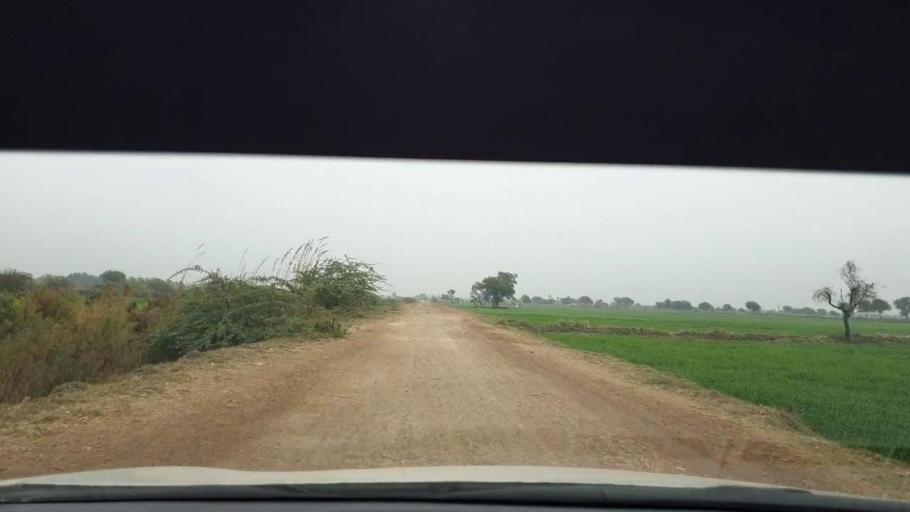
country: PK
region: Sindh
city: Berani
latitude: 25.7618
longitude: 68.8402
